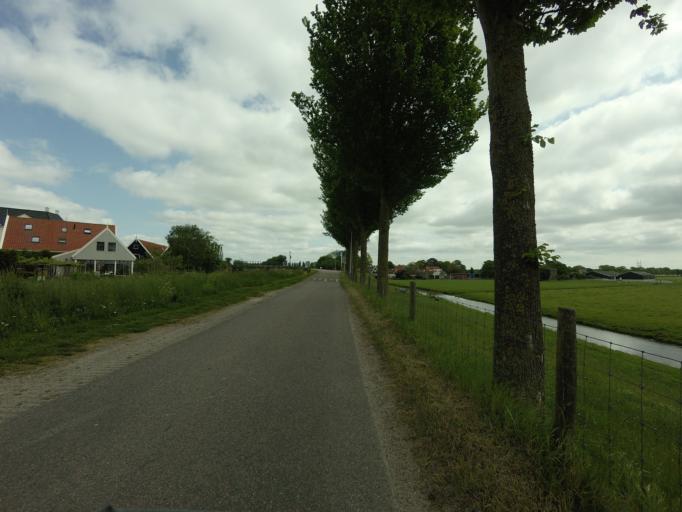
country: NL
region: North Holland
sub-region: Gemeente Beemster
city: Halfweg
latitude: 52.5590
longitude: 4.8581
